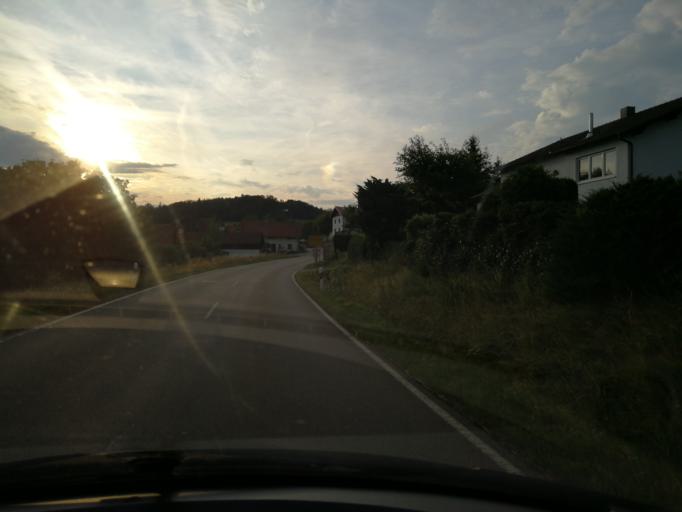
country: DE
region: Bavaria
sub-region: Upper Palatinate
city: Falkenstein
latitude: 49.0887
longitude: 12.5024
